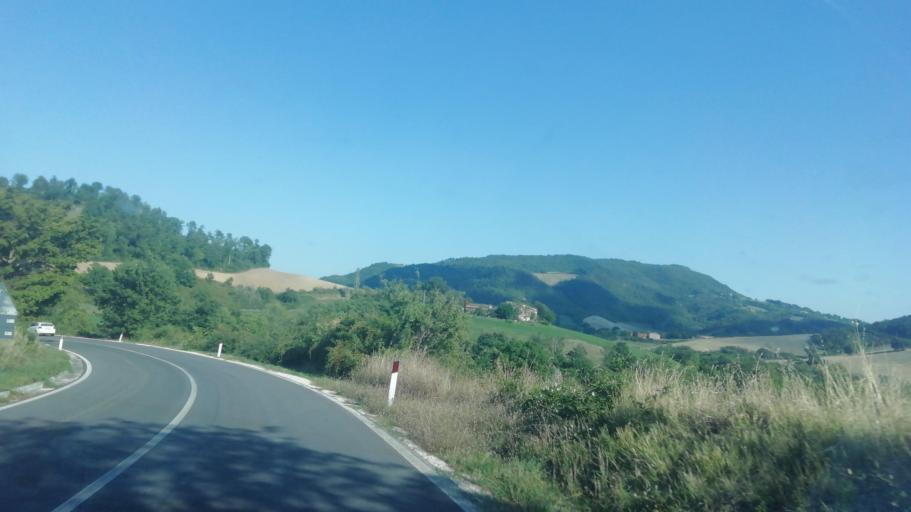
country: IT
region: The Marches
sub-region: Provincia di Pesaro e Urbino
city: Frontone
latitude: 43.5376
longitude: 12.7432
